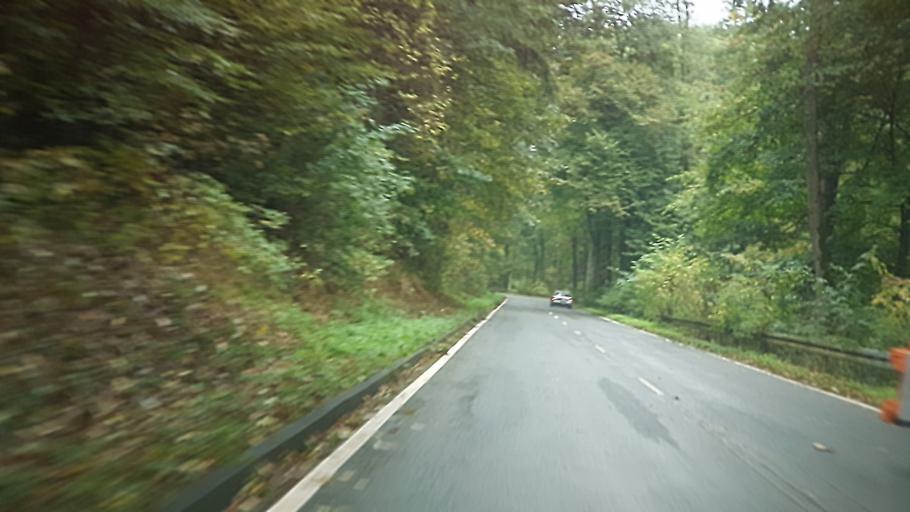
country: DE
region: North Rhine-Westphalia
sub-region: Regierungsbezirk Arnsberg
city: Luedenscheid
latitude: 51.1825
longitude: 7.6780
